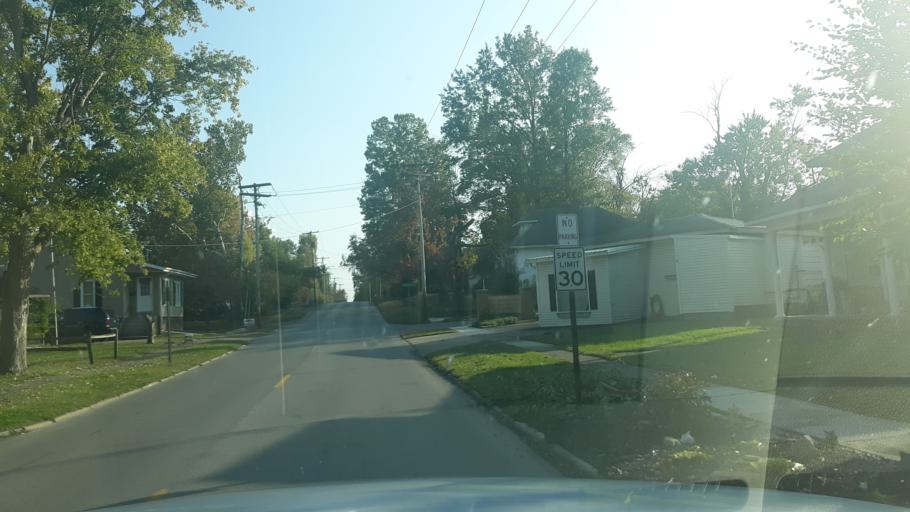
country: US
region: Illinois
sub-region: Saline County
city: Harrisburg
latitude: 37.7289
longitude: -88.5403
